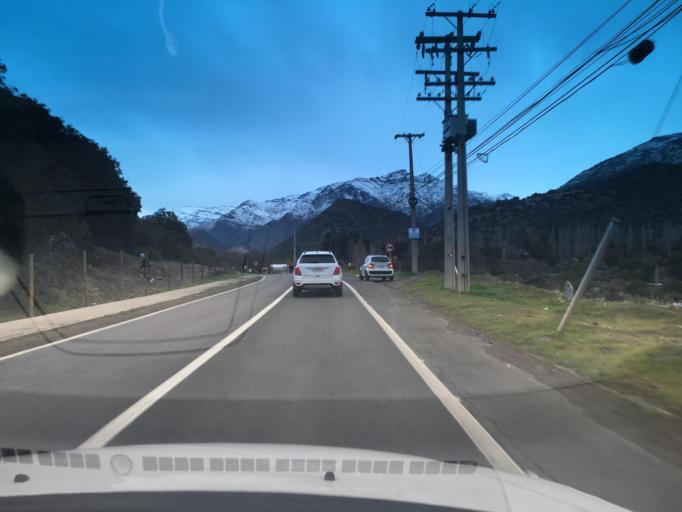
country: CL
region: Santiago Metropolitan
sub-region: Provincia de Cordillera
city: Puente Alto
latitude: -33.6705
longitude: -70.3477
